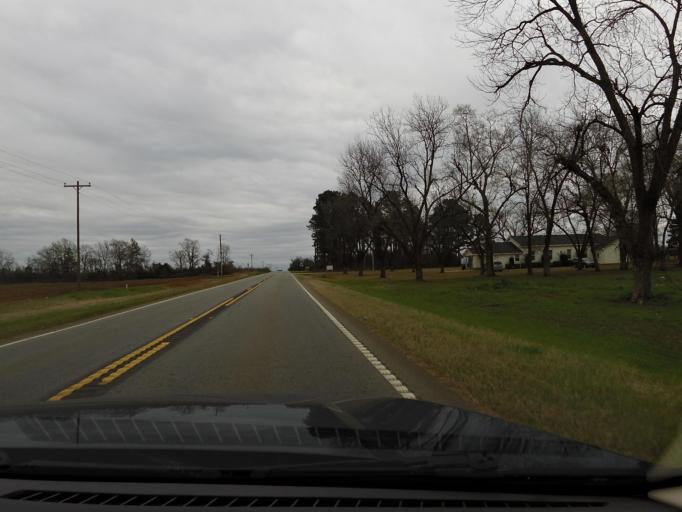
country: US
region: Georgia
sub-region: Randolph County
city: Shellman
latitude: 31.7729
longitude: -84.6827
